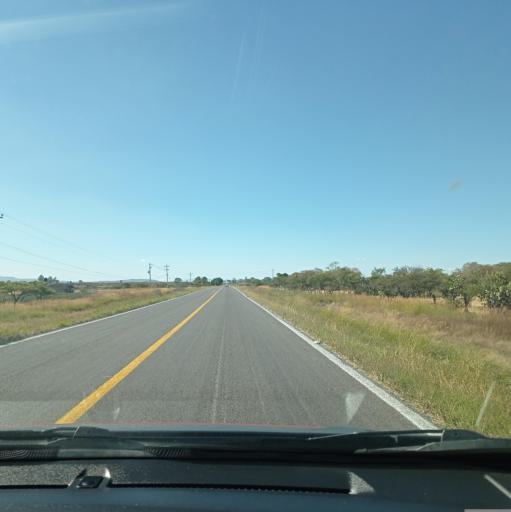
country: MX
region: Jalisco
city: Valle de Guadalupe
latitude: 21.0200
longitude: -102.5300
